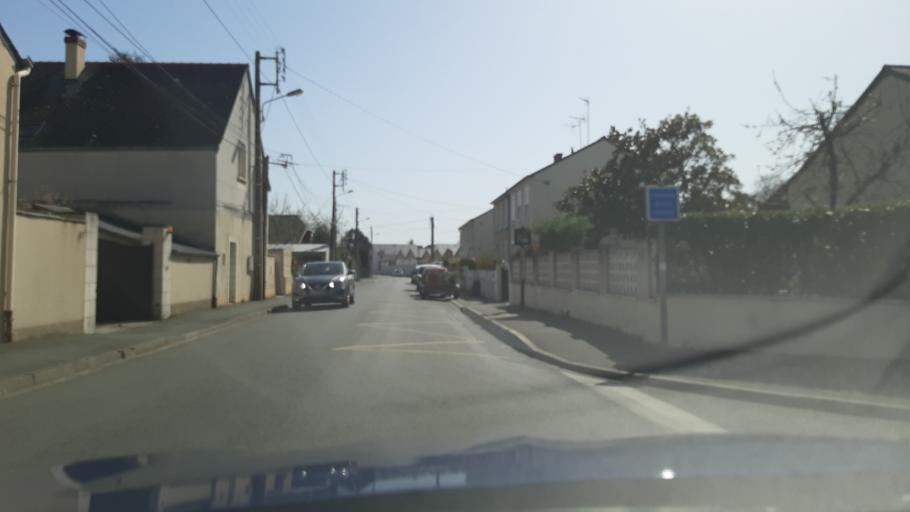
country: FR
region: Pays de la Loire
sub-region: Departement de Maine-et-Loire
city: Les Ponts-de-Ce
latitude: 47.4028
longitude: -0.5252
